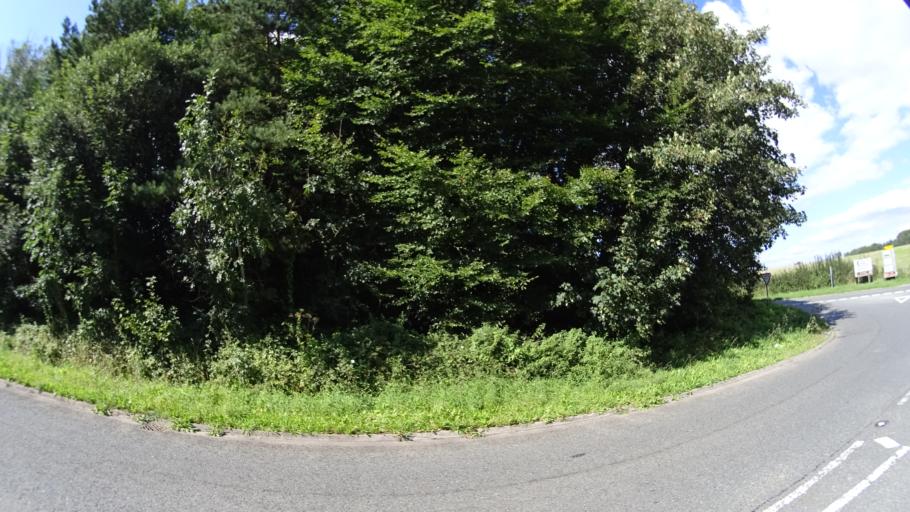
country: GB
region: England
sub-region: Wiltshire
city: Mere
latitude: 51.0908
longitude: -2.2972
